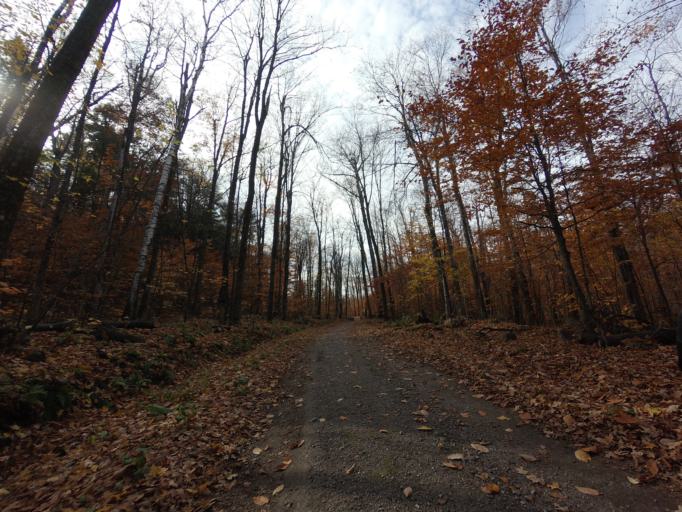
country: CA
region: Quebec
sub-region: Outaouais
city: Wakefield
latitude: 45.5347
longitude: -75.9332
